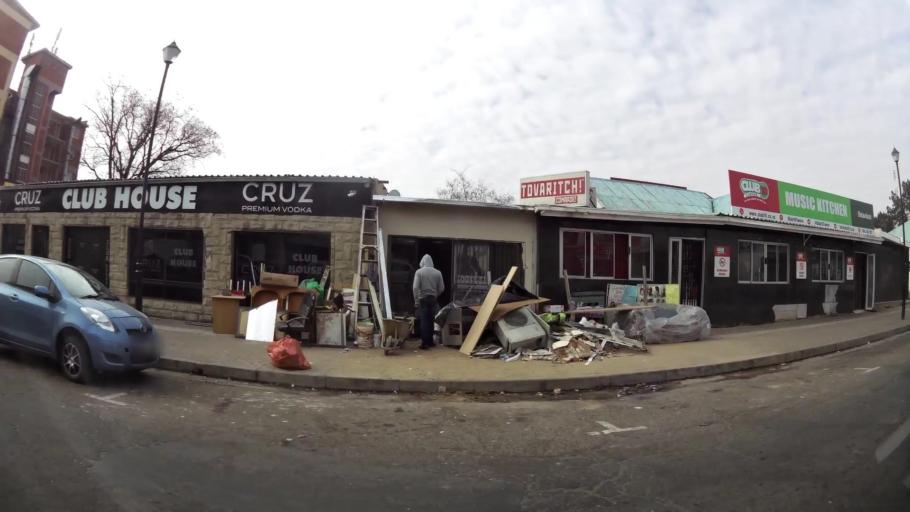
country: ZA
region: Orange Free State
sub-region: Mangaung Metropolitan Municipality
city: Bloemfontein
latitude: -29.1211
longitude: 26.2079
